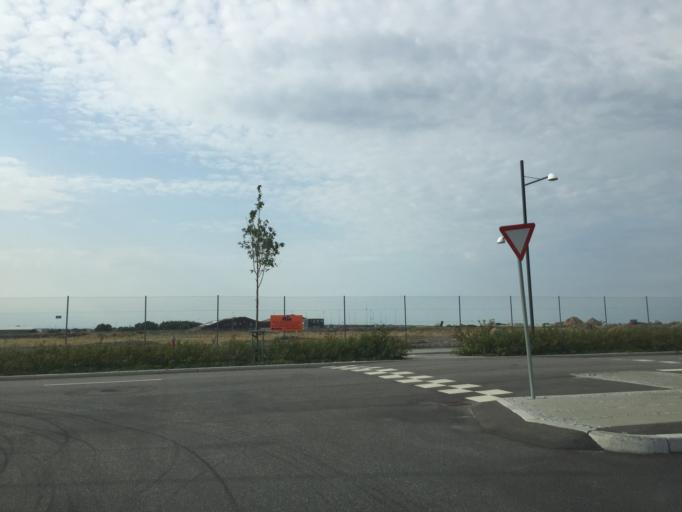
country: DK
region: Capital Region
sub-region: Kobenhavn
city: Christianshavn
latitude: 55.7150
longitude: 12.6226
